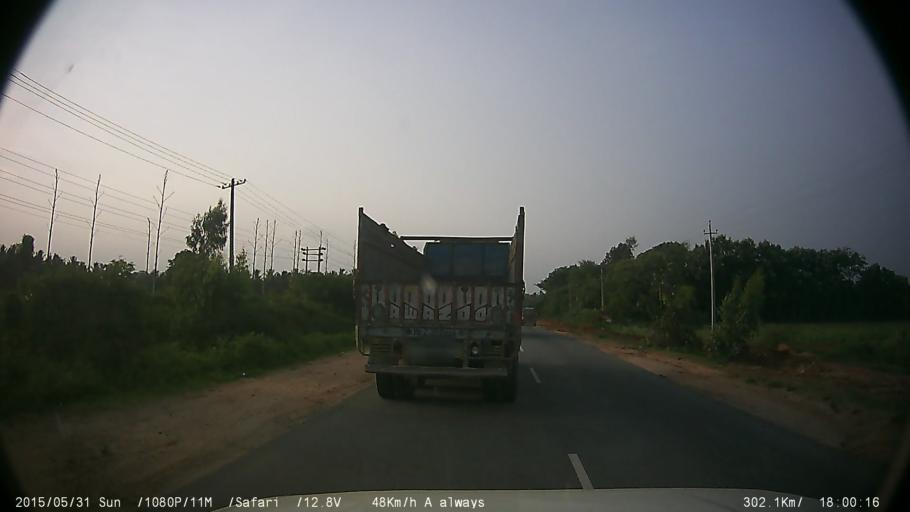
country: IN
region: Karnataka
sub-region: Mysore
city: Nanjangud
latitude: 12.0199
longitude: 76.6728
